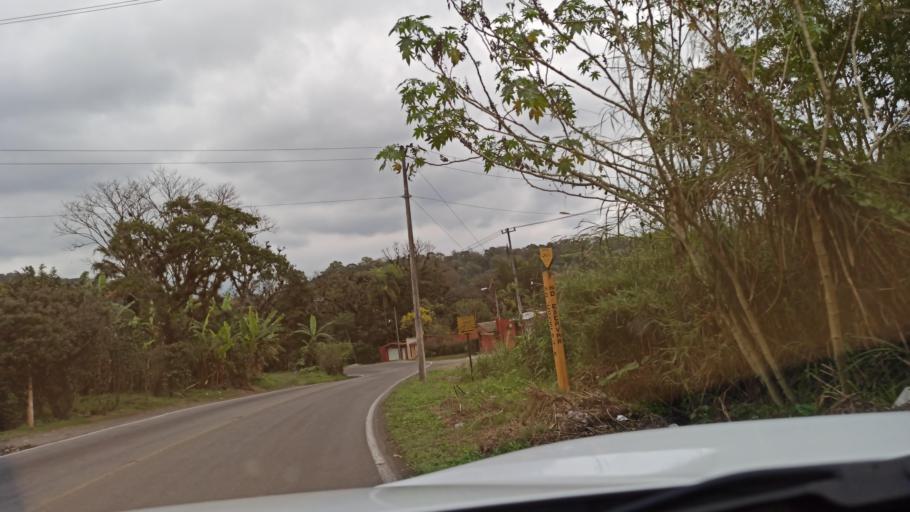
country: MX
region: Veracruz
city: Cuautlapan
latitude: 18.8915
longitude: -97.0122
